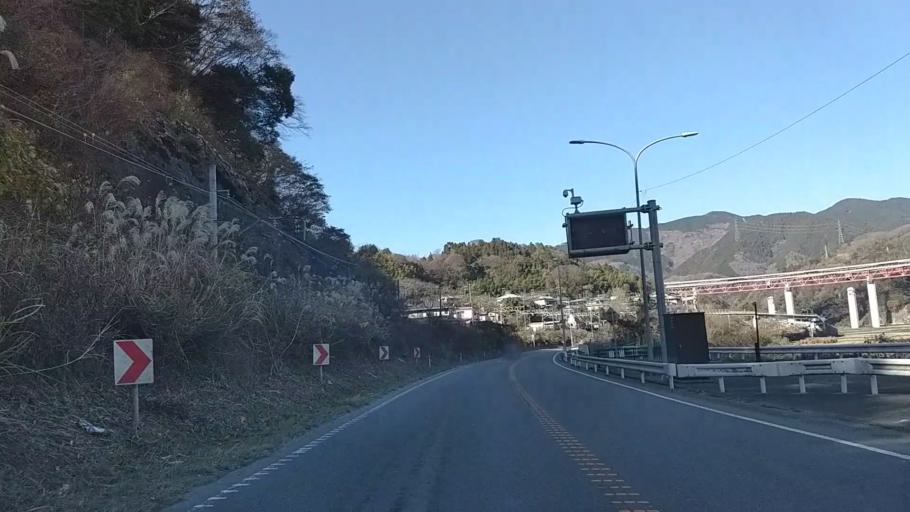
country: JP
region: Shizuoka
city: Gotemba
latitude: 35.3634
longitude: 139.0411
